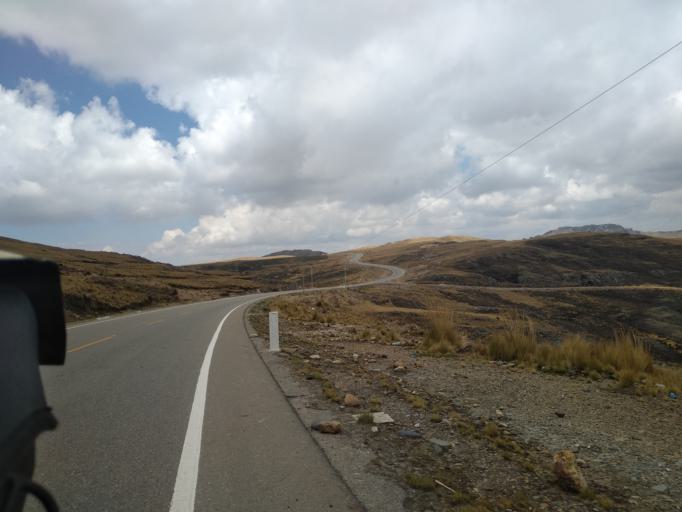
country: PE
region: La Libertad
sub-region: Provincia de Santiago de Chuco
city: Quiruvilca
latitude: -7.9594
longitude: -78.1958
